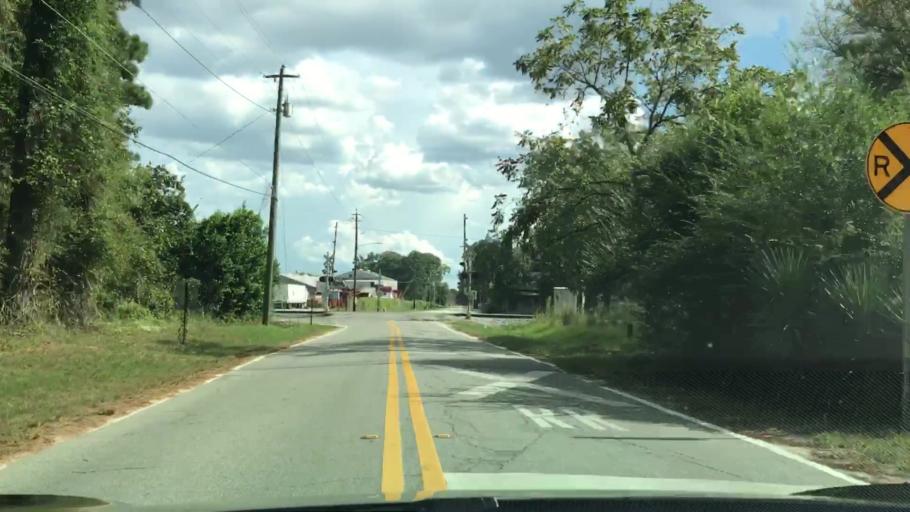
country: US
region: Georgia
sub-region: Jefferson County
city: Wadley
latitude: 32.8628
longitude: -82.3975
